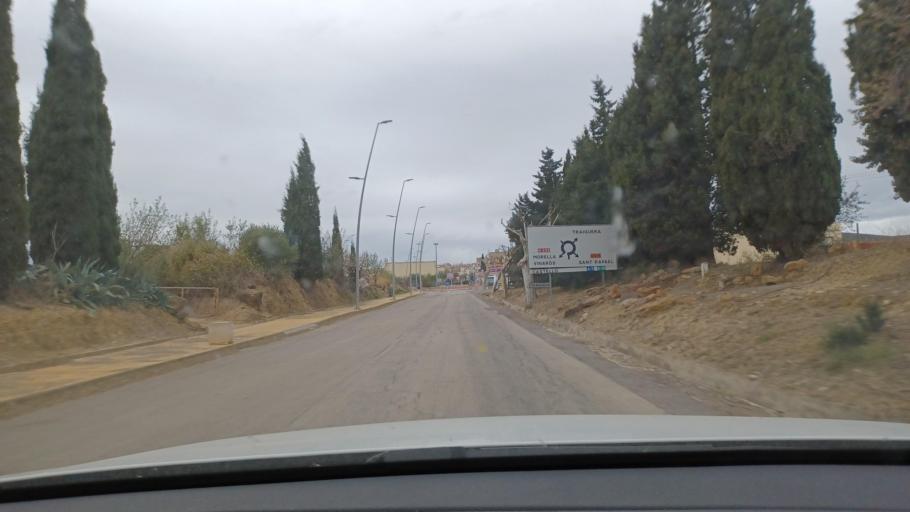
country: ES
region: Valencia
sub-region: Provincia de Castello
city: Traiguera
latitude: 40.5252
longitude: 0.2967
